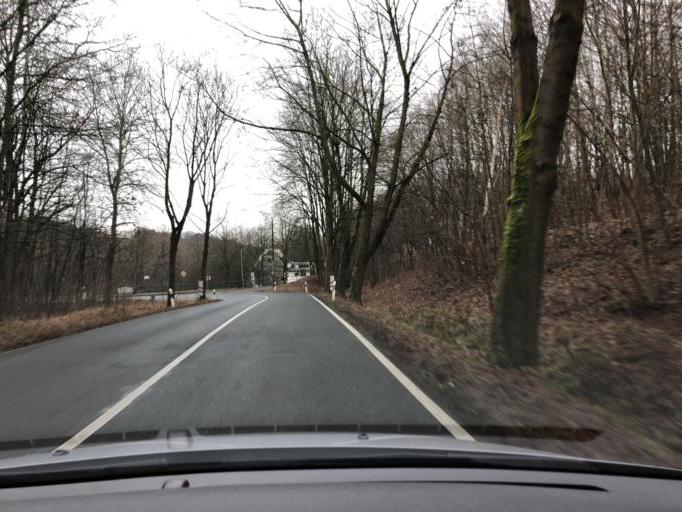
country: DE
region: Saxony
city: Niederstriegis
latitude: 51.0748
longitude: 13.1530
